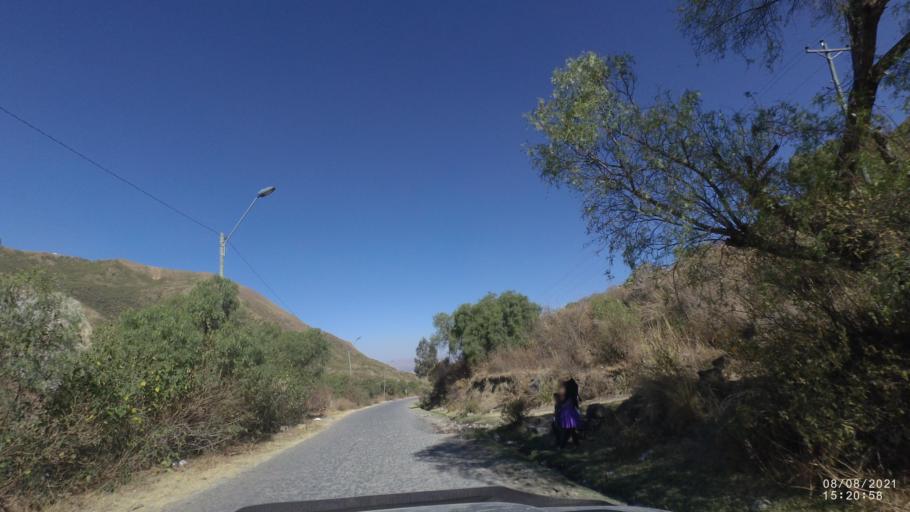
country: BO
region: Cochabamba
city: Cochabamba
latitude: -17.2991
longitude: -66.2964
